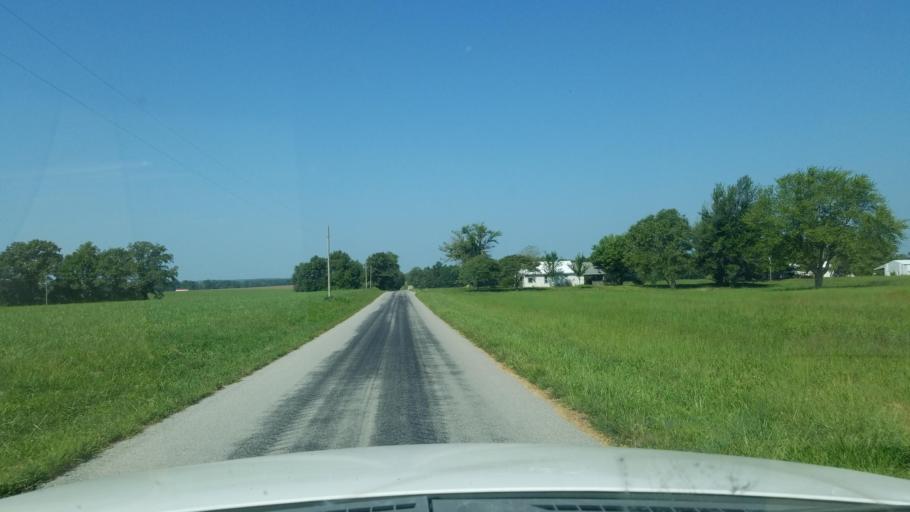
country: US
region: Illinois
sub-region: Saline County
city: Harrisburg
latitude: 37.8922
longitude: -88.6584
